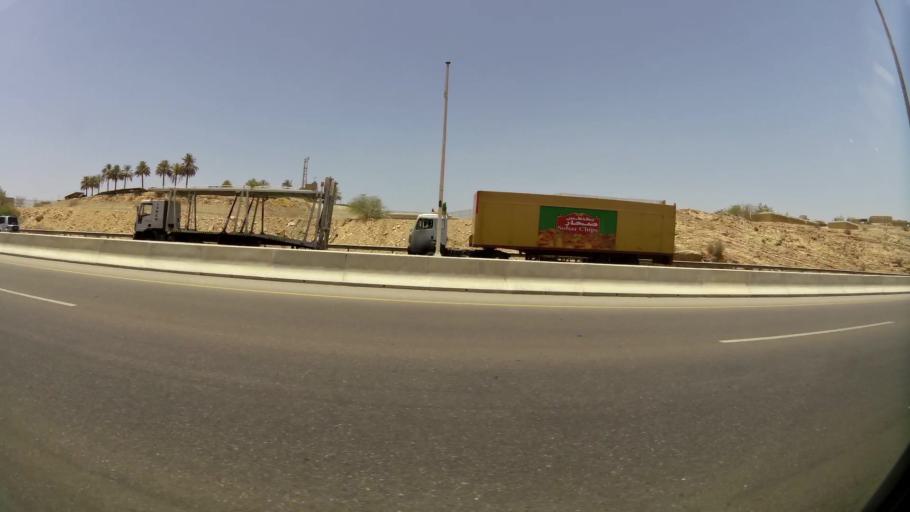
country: OM
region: Muhafazat Masqat
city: Bawshar
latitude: 23.5991
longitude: 58.4818
